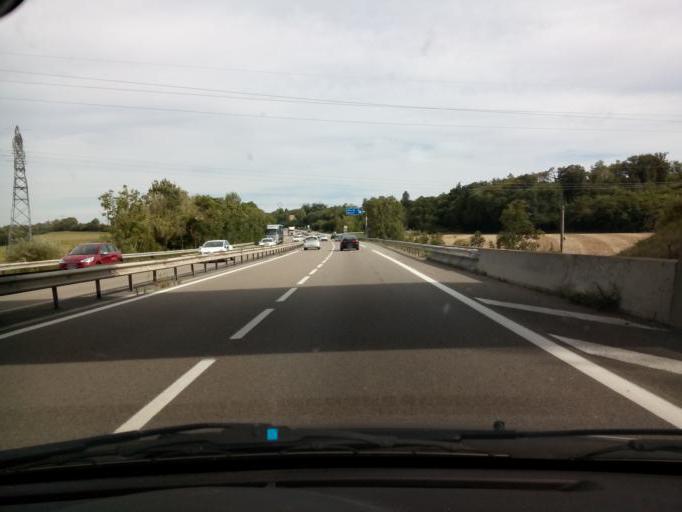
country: FR
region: Rhone-Alpes
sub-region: Departement de l'Isere
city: Chabons
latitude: 45.4271
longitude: 5.4316
